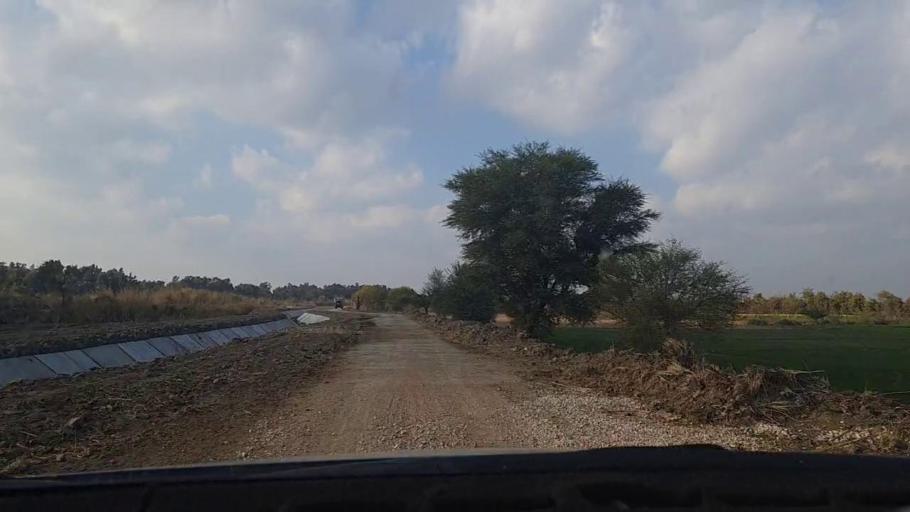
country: PK
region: Sindh
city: Tando Mittha Khan
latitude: 25.9099
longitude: 69.3072
